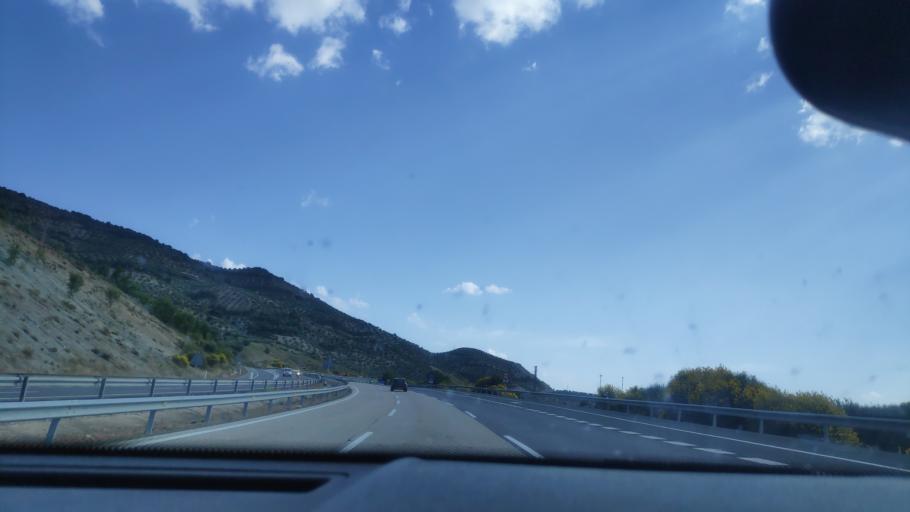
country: ES
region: Andalusia
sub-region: Provincia de Jaen
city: Campillo de Arenas
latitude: 37.5613
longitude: -3.6256
